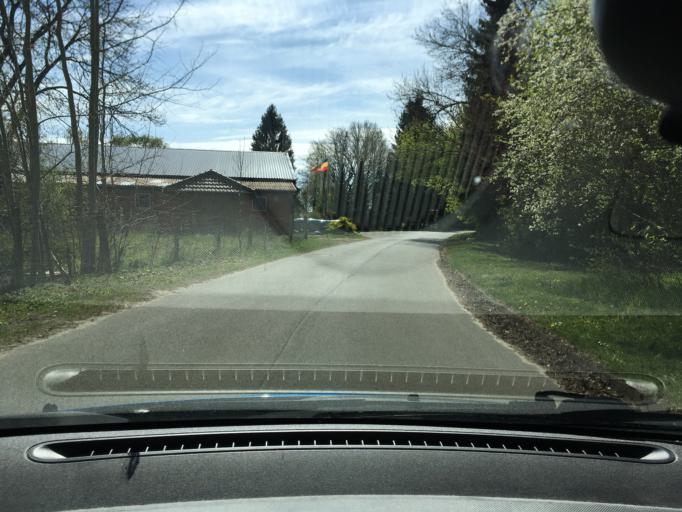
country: DE
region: Lower Saxony
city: Himbergen
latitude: 53.1259
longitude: 10.7049
